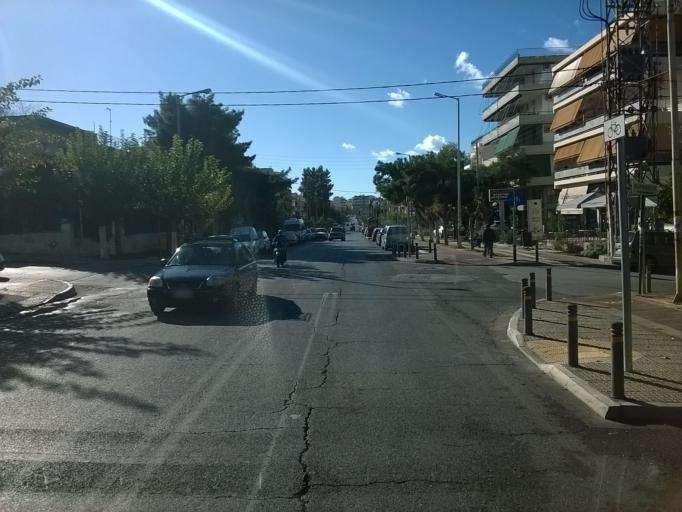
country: GR
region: Attica
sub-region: Nomarchia Athinas
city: Argyroupoli
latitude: 37.9045
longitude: 23.7503
